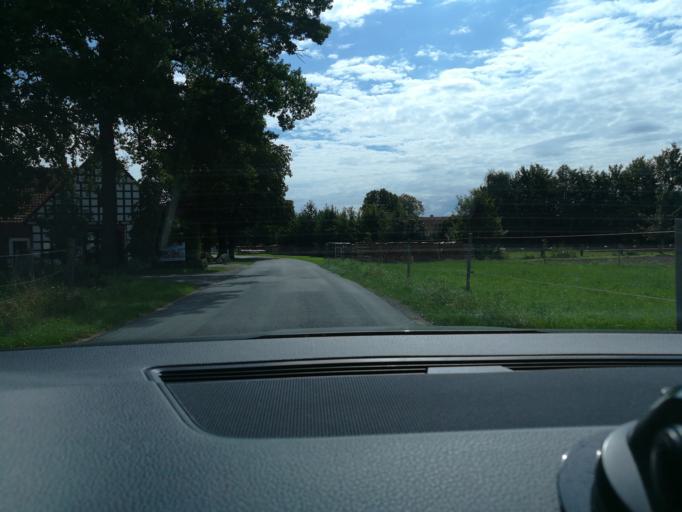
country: DE
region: North Rhine-Westphalia
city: Espelkamp
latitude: 52.3481
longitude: 8.6699
